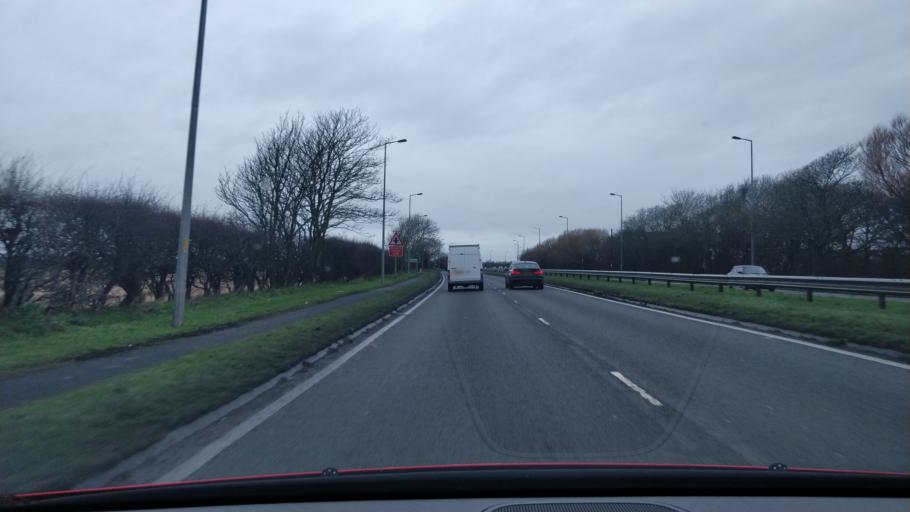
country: GB
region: England
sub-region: Sefton
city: Ince Blundell
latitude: 53.5345
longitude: -3.0424
